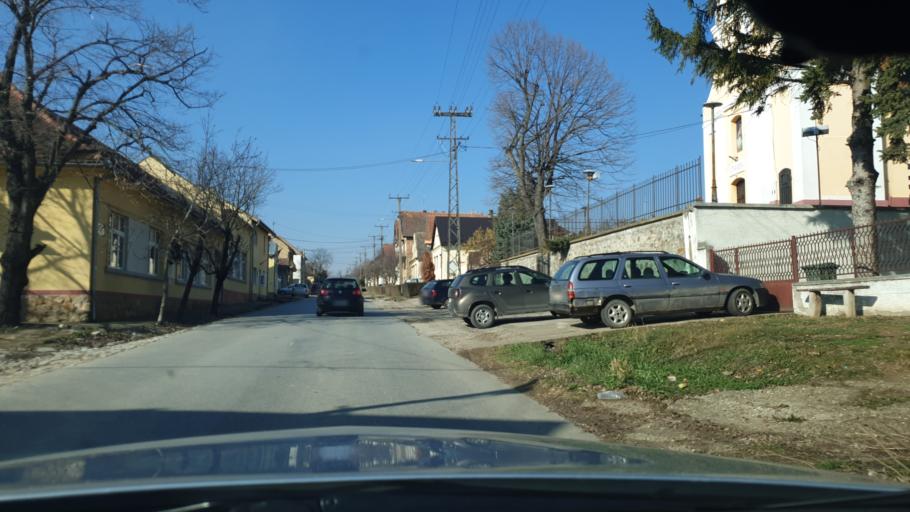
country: RS
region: Autonomna Pokrajina Vojvodina
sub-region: Sremski Okrug
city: Irig
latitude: 45.0887
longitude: 19.8351
